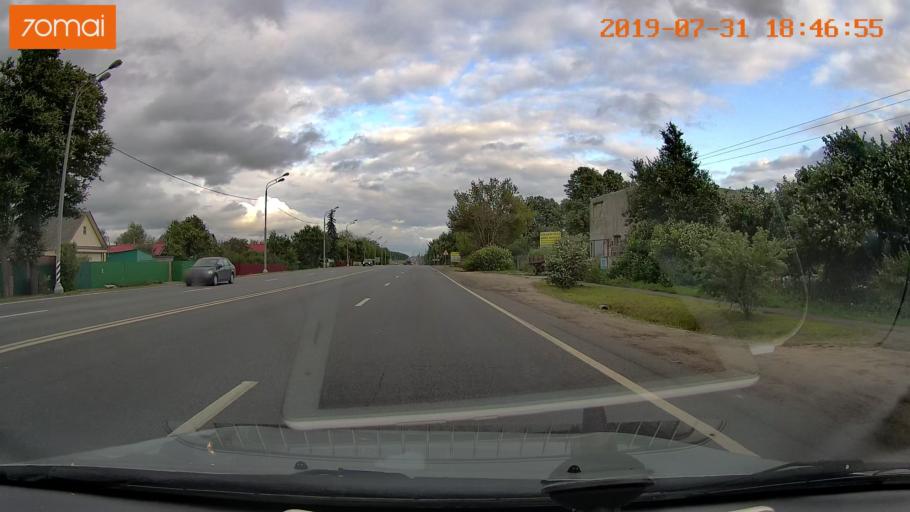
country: RU
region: Moskovskaya
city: Troitskoye
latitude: 55.2430
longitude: 38.5354
